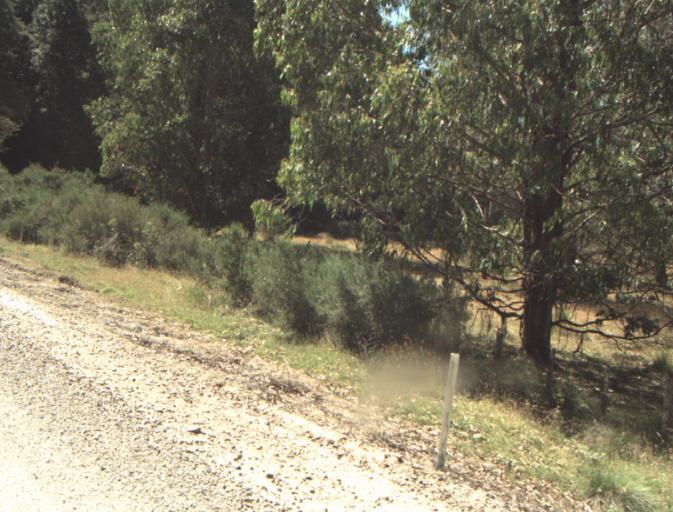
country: AU
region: Tasmania
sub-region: Dorset
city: Scottsdale
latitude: -41.3651
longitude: 147.4668
